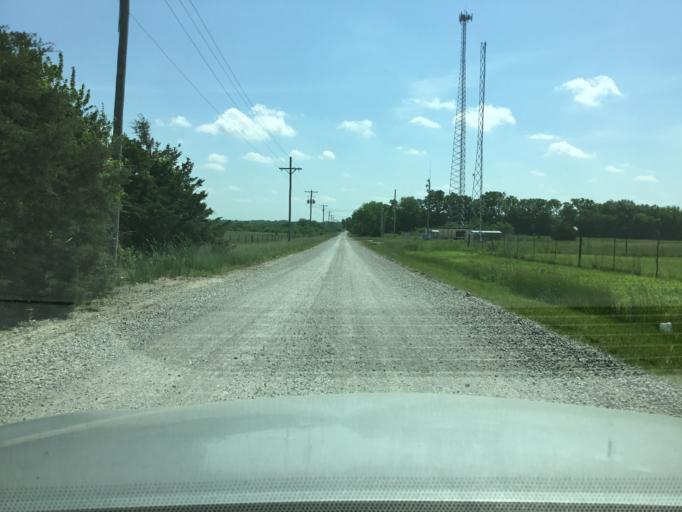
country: US
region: Kansas
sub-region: Labette County
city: Parsons
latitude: 37.3109
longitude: -95.2654
